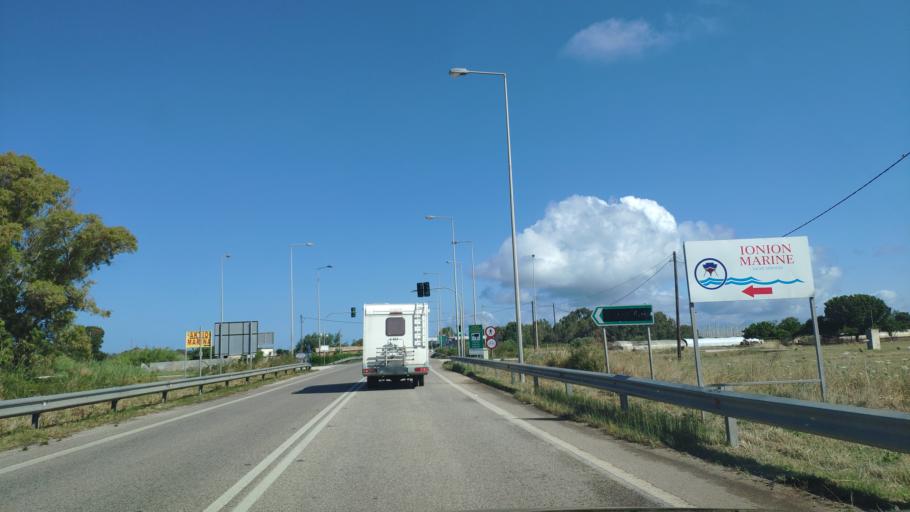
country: GR
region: Epirus
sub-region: Nomos Prevezis
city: Preveza
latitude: 38.9371
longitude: 20.7684
